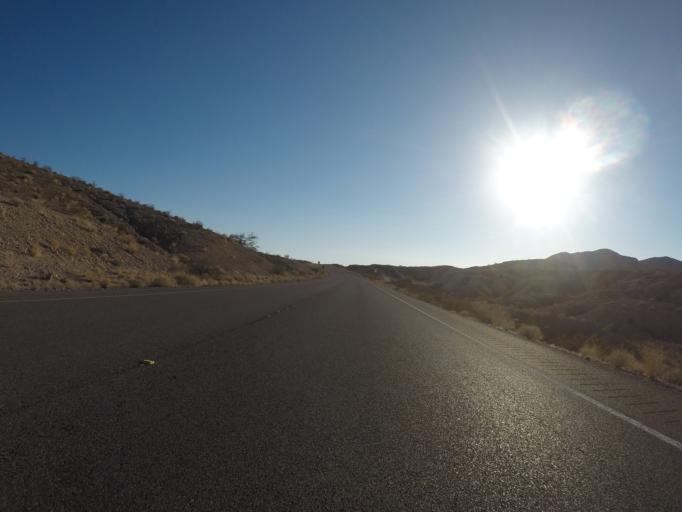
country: US
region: Nevada
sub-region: Clark County
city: Moapa Valley
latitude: 36.3982
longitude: -114.4232
